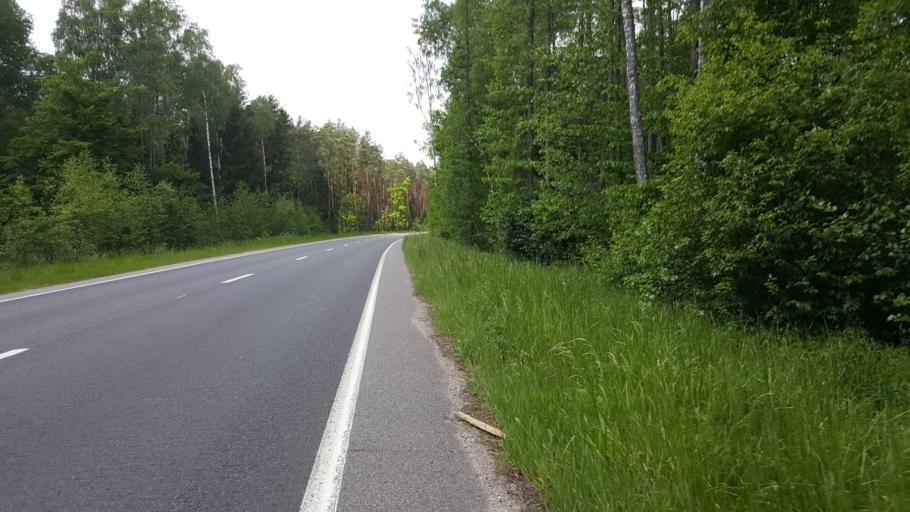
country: PL
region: Podlasie
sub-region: Powiat hajnowski
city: Bialowieza
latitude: 52.5664
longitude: 24.1134
